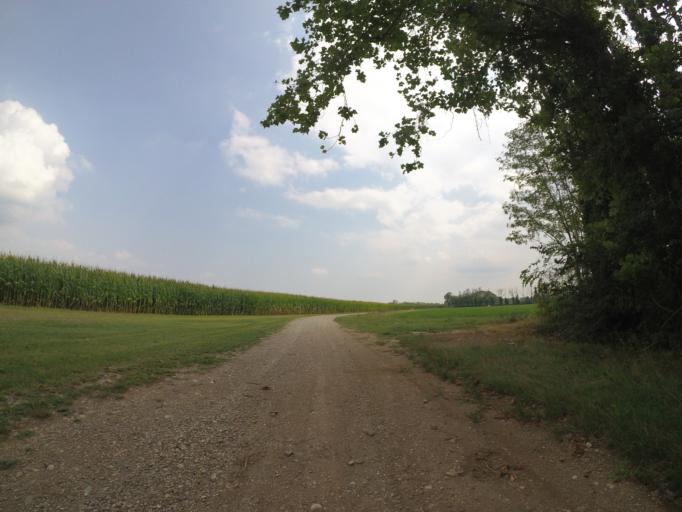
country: IT
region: Friuli Venezia Giulia
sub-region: Provincia di Udine
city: Codroipo
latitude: 45.9818
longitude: 13.0019
